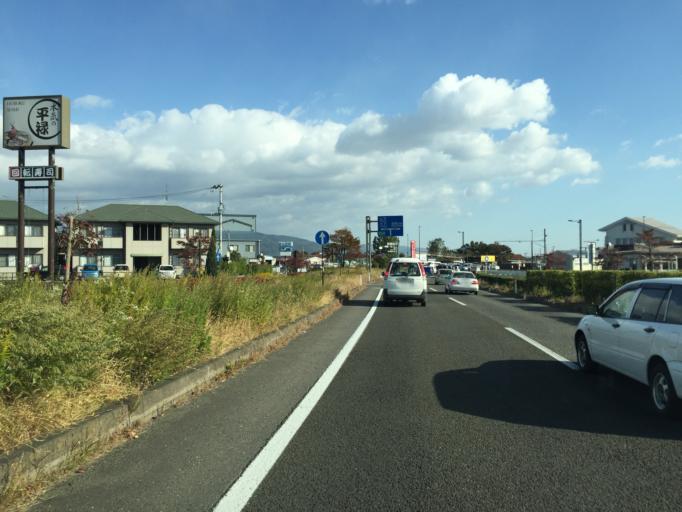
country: JP
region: Fukushima
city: Fukushima-shi
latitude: 37.7893
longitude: 140.4601
